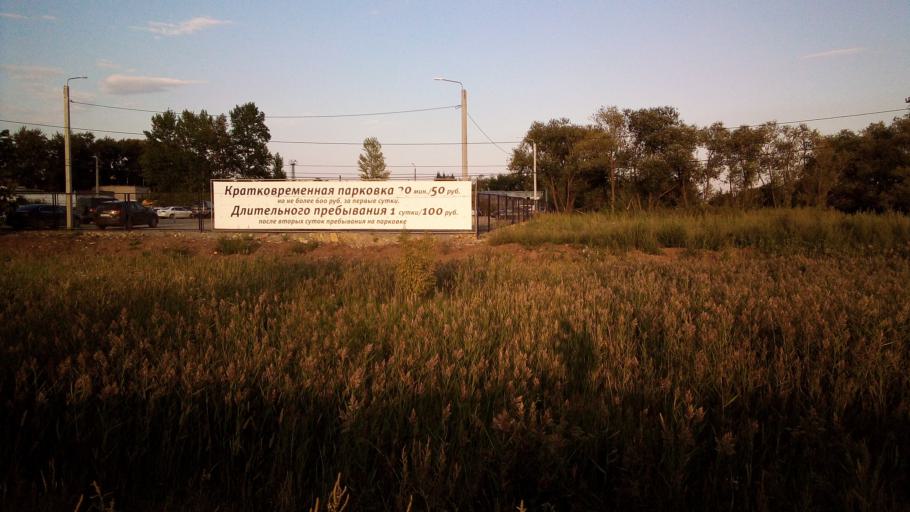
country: RU
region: Chelyabinsk
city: Potanino
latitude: 55.2941
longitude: 61.5116
